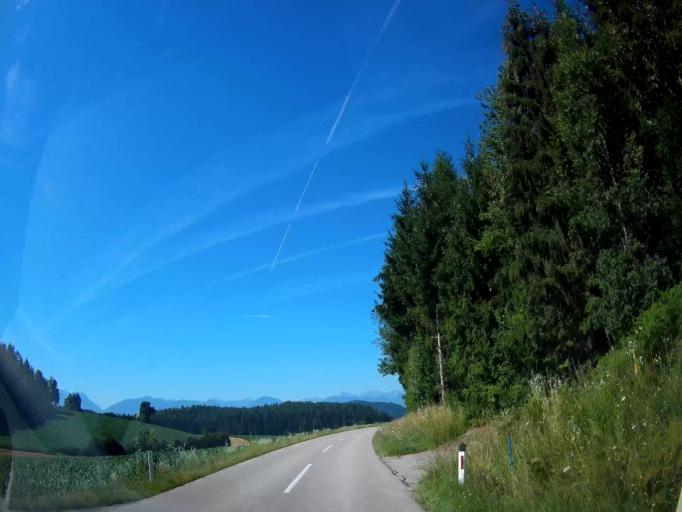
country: AT
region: Carinthia
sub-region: Politischer Bezirk Klagenfurt Land
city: Maria Saal
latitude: 46.6987
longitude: 14.3954
